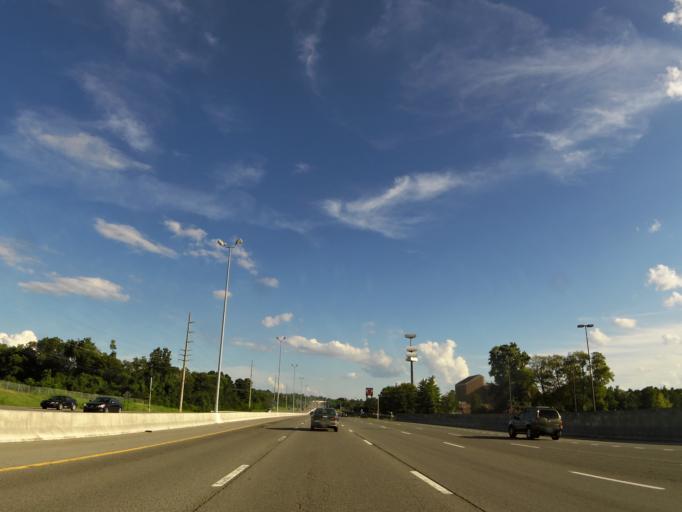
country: US
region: Tennessee
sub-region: Davidson County
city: Lakewood
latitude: 36.2110
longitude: -86.6913
